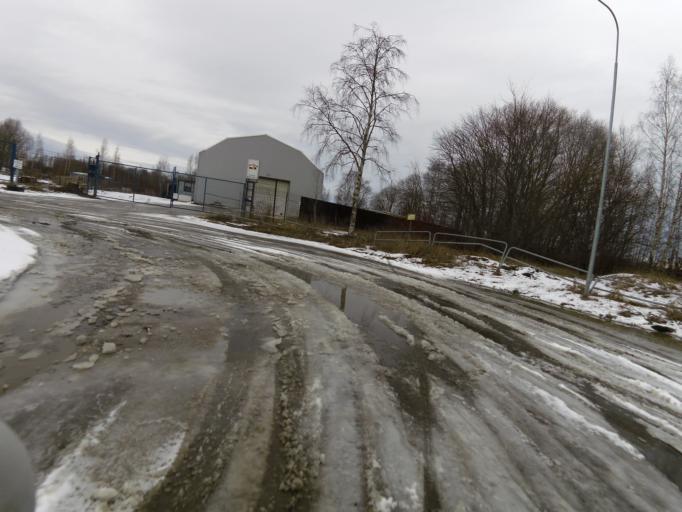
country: SE
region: Gaevleborg
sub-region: Gavle Kommun
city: Gavle
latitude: 60.6847
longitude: 17.1658
